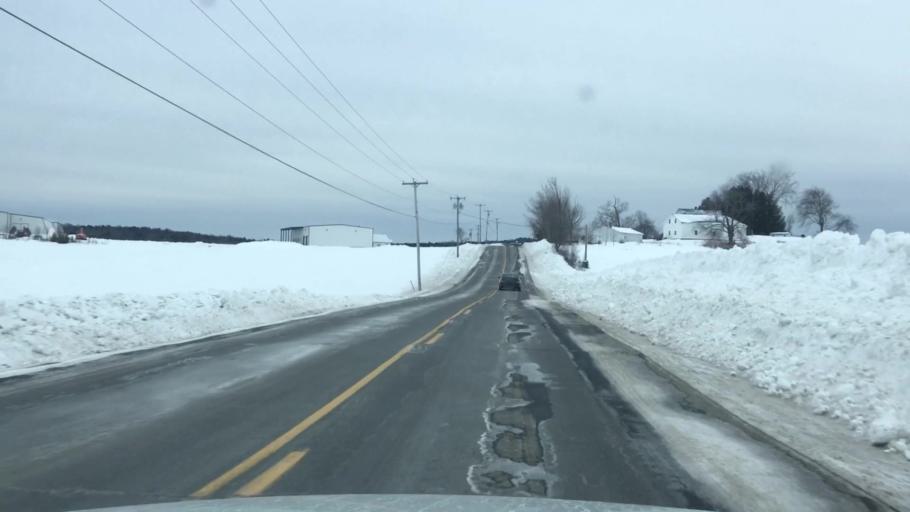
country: US
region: Maine
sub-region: Penobscot County
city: Garland
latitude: 44.9795
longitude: -69.0894
